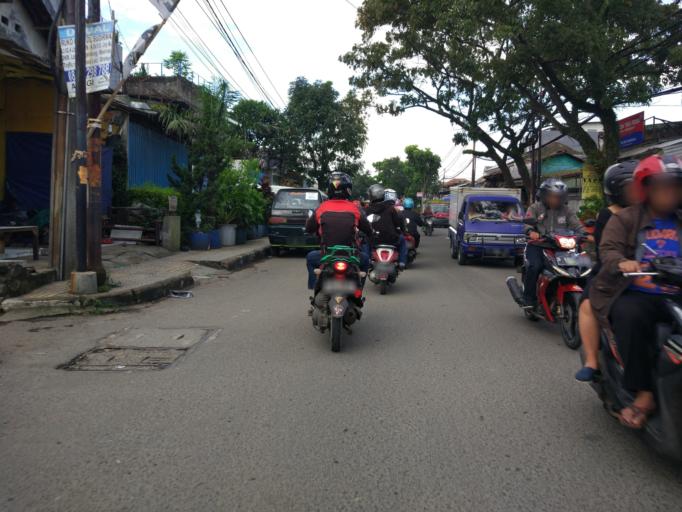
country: ID
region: West Java
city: Bandung
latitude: -6.9219
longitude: 107.5842
